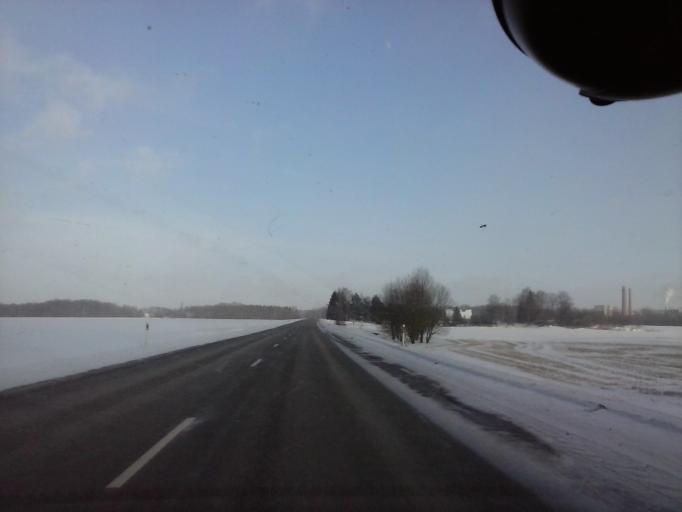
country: EE
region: Tartu
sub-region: Puhja vald
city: Puhja
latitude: 58.3282
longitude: 26.2816
